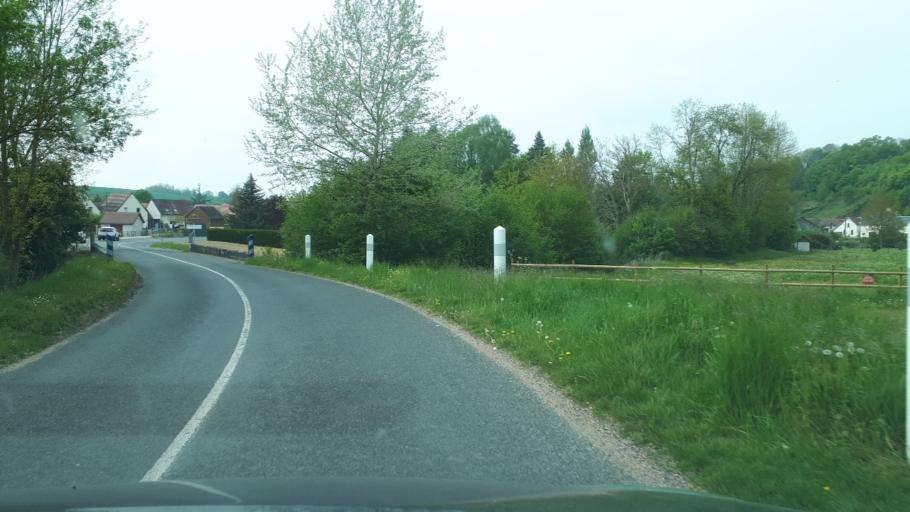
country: FR
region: Centre
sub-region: Departement du Loir-et-Cher
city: Lunay
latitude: 47.8202
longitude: 0.9493
